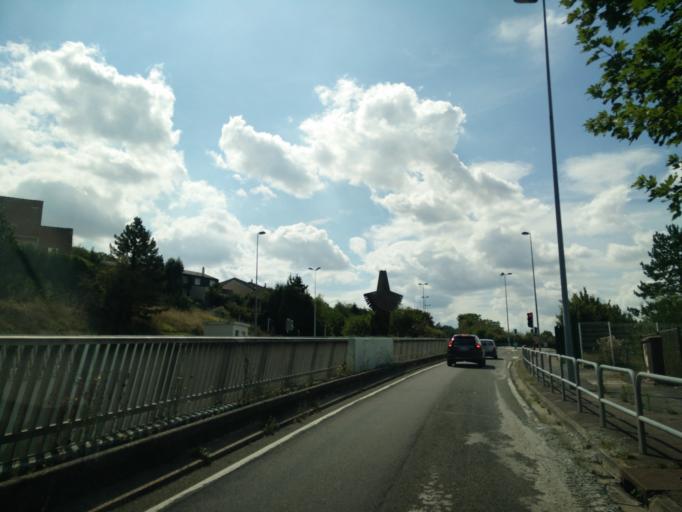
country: FR
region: Ile-de-France
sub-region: Departement des Yvelines
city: Mantes-la-Ville
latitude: 48.9642
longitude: 1.7171
